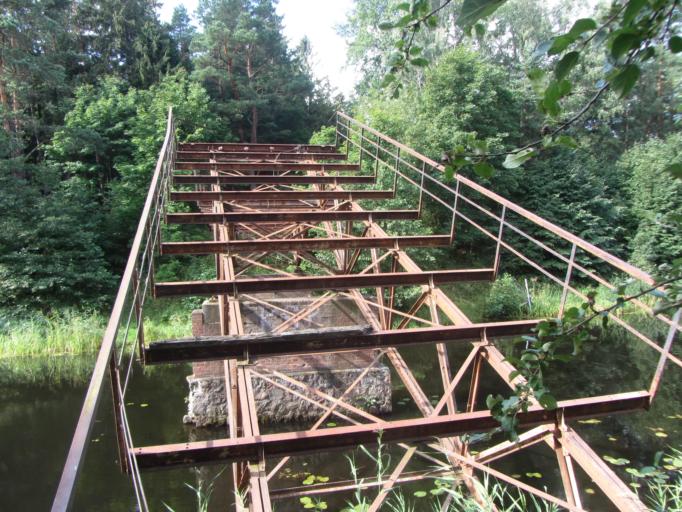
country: LT
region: Klaipedos apskritis
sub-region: Klaipeda
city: Klaipeda
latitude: 55.6134
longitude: 21.1937
